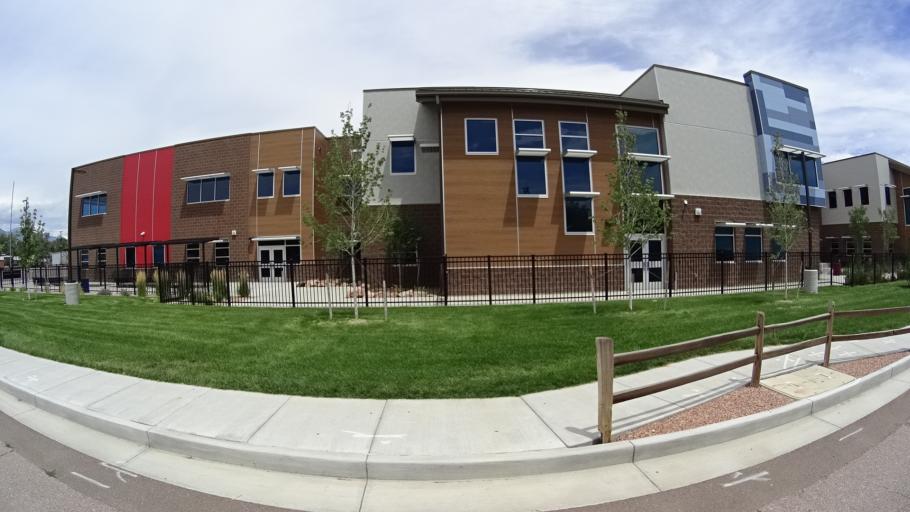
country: US
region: Colorado
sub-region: El Paso County
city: Fountain
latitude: 38.6855
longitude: -104.7075
